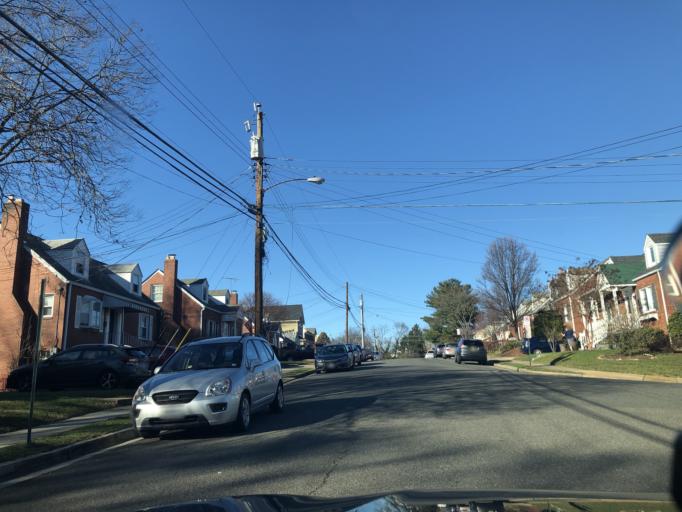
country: US
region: Virginia
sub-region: Arlington County
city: Arlington
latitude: 38.8770
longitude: -77.1189
